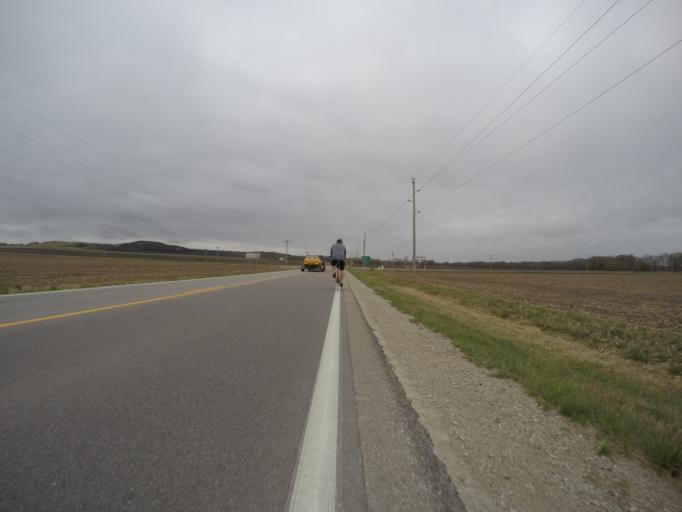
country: US
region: Kansas
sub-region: Pottawatomie County
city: Wamego
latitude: 39.1534
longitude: -96.3057
